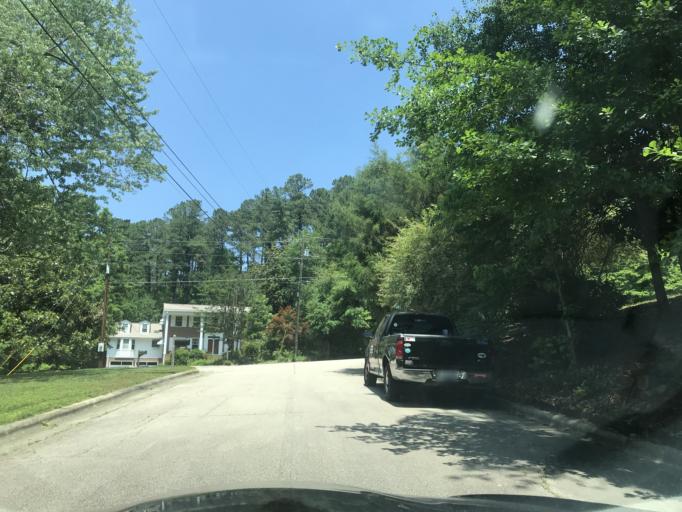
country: US
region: North Carolina
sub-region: Wake County
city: West Raleigh
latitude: 35.8423
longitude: -78.6605
